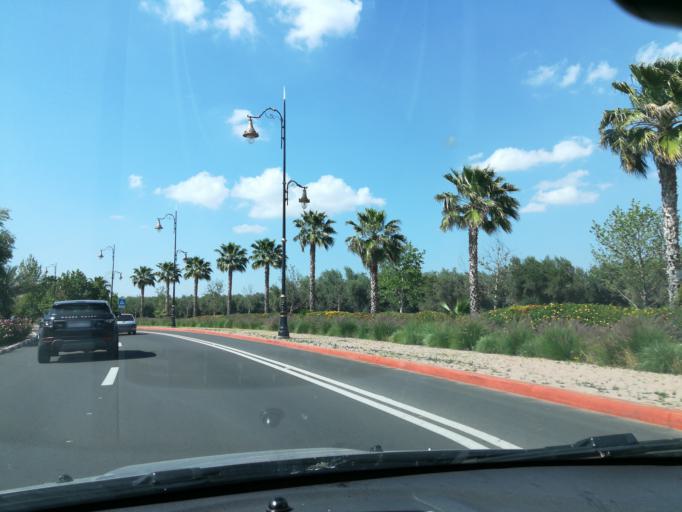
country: MA
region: Marrakech-Tensift-Al Haouz
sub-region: Marrakech
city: Marrakesh
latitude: 31.6142
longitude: -8.0040
